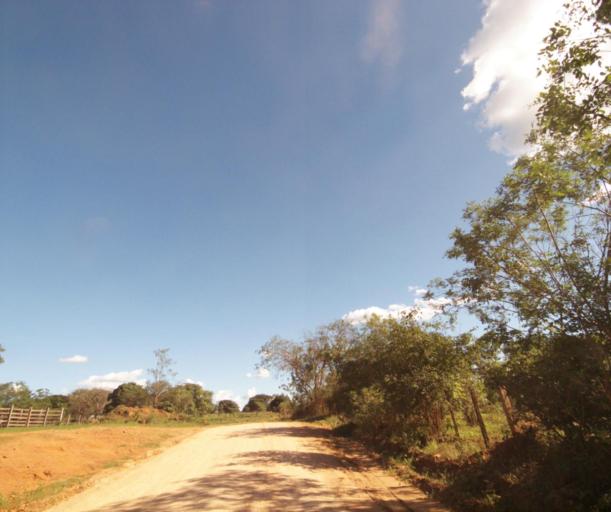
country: BR
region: Bahia
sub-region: Carinhanha
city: Carinhanha
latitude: -14.2059
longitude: -44.5418
